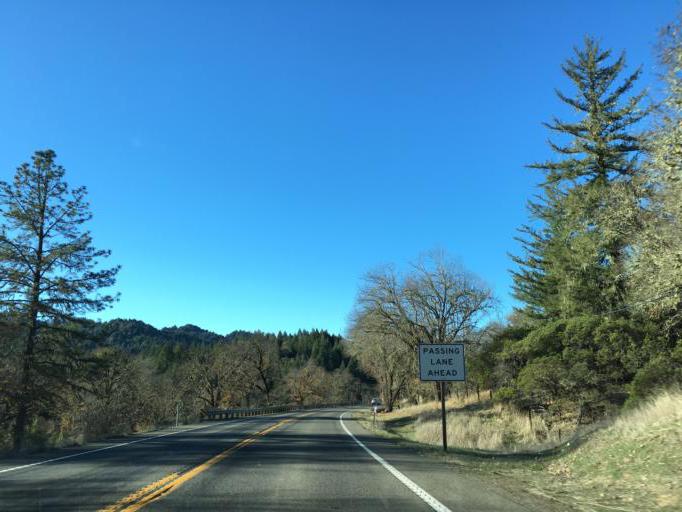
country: US
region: California
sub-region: Mendocino County
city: Laytonville
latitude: 39.7493
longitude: -123.5318
